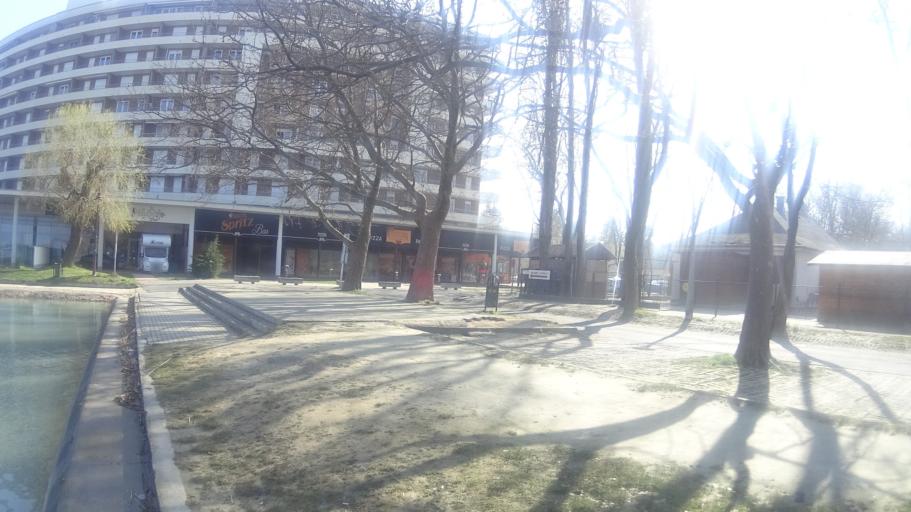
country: HU
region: Somogy
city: Siofok
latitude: 46.9148
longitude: 18.0629
